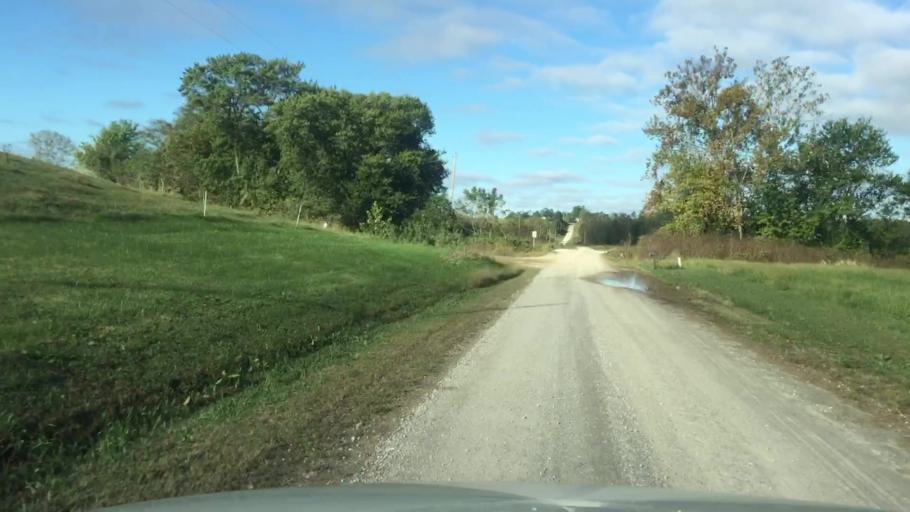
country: US
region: Missouri
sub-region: Howard County
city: New Franklin
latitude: 39.0832
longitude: -92.7647
